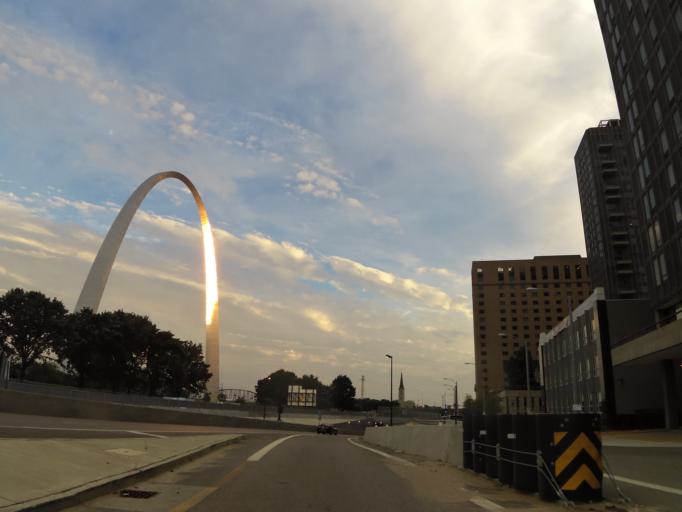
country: US
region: Missouri
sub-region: City of Saint Louis
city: St. Louis
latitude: 38.6279
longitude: -90.1863
